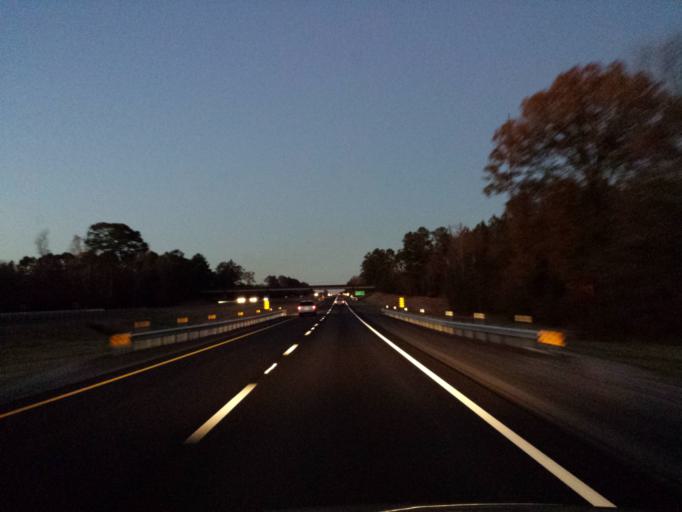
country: US
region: Mississippi
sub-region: Jones County
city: Sharon
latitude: 31.8108
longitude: -89.0527
